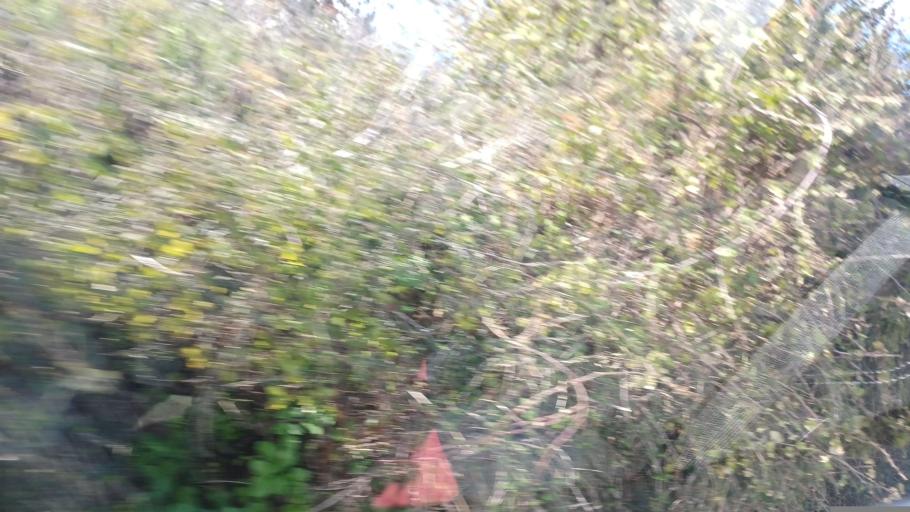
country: CY
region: Pafos
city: Mesogi
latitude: 34.8358
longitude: 32.5503
